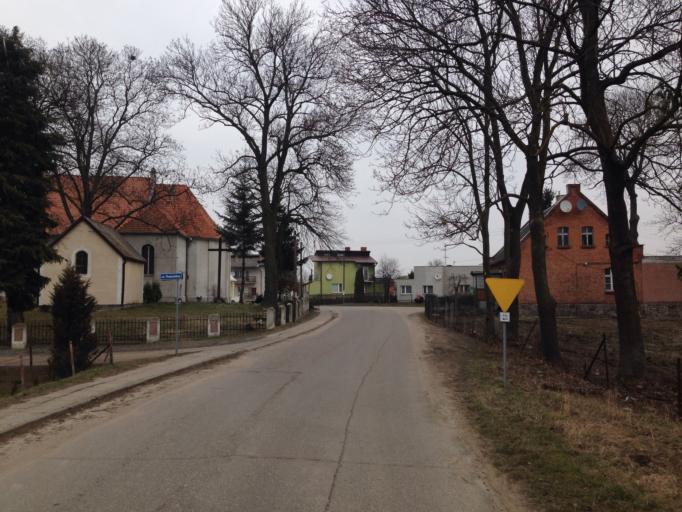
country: PL
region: Pomeranian Voivodeship
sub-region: Powiat kwidzynski
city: Sadlinki
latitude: 53.7415
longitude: 18.8241
